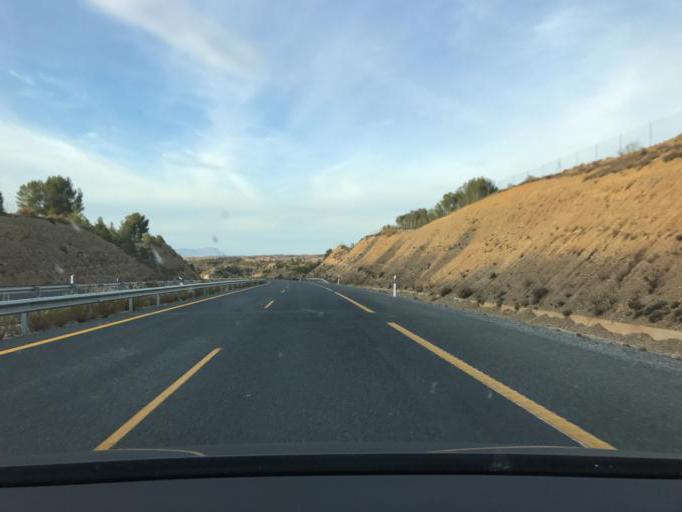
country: ES
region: Andalusia
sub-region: Provincia de Granada
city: Guadix
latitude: 37.2755
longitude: -3.0954
